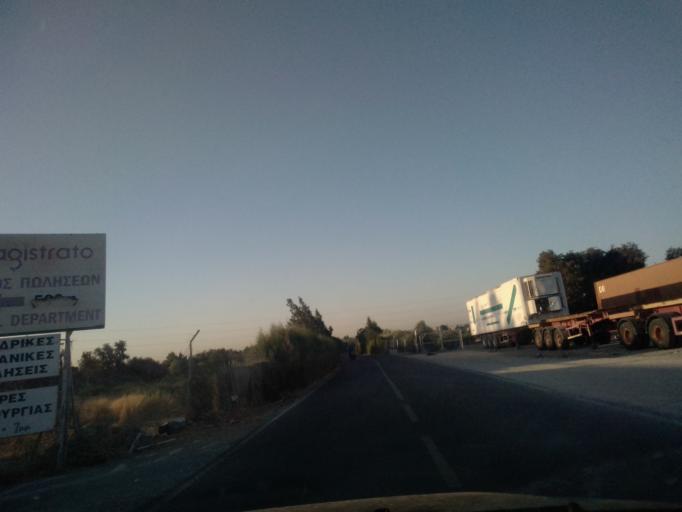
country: CY
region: Limassol
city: Ypsonas
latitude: 34.6678
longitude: 32.9613
